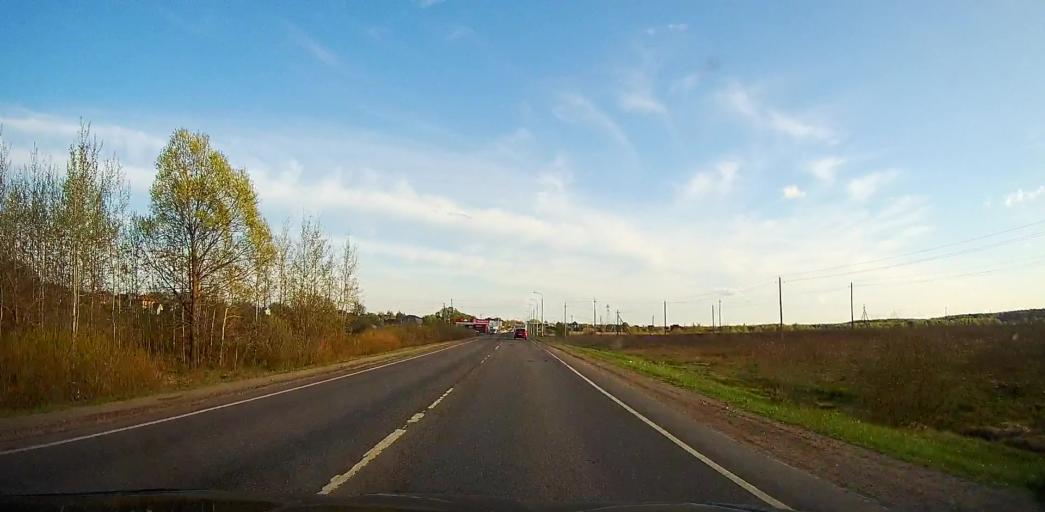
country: RU
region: Moskovskaya
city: Bronnitsy
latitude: 55.3329
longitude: 38.2197
